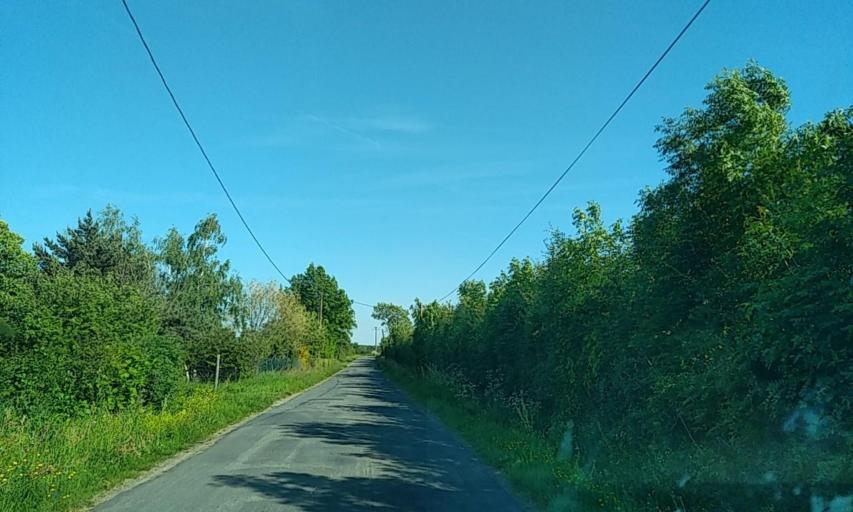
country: FR
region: Poitou-Charentes
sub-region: Departement des Deux-Sevres
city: Boisme
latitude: 46.7997
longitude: -0.4391
